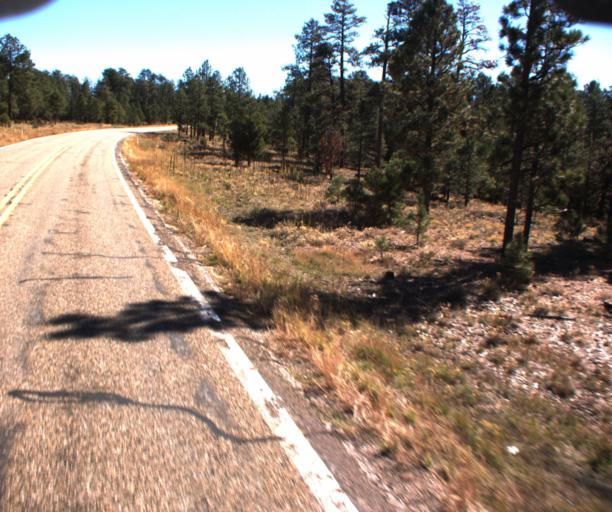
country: US
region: Arizona
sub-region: Coconino County
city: Fredonia
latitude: 36.7435
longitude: -112.2352
